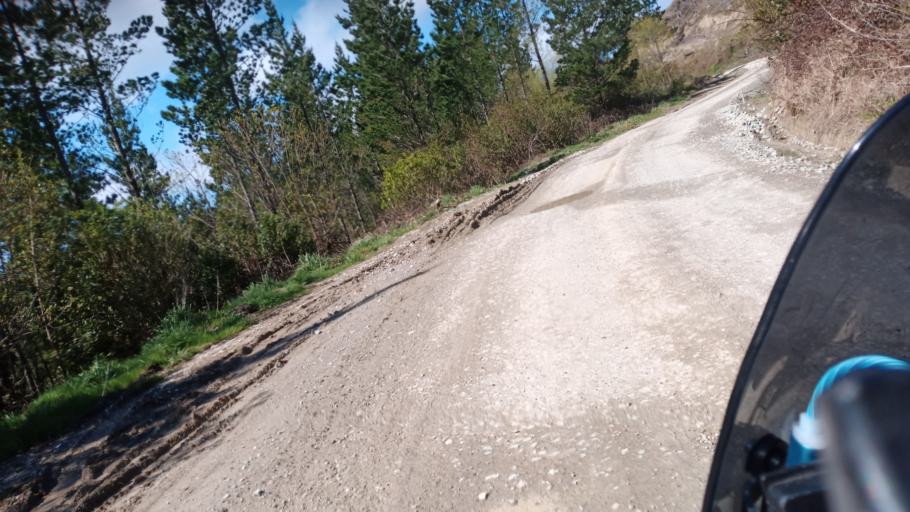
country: NZ
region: Gisborne
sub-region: Gisborne District
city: Gisborne
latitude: -38.9071
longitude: 177.8106
